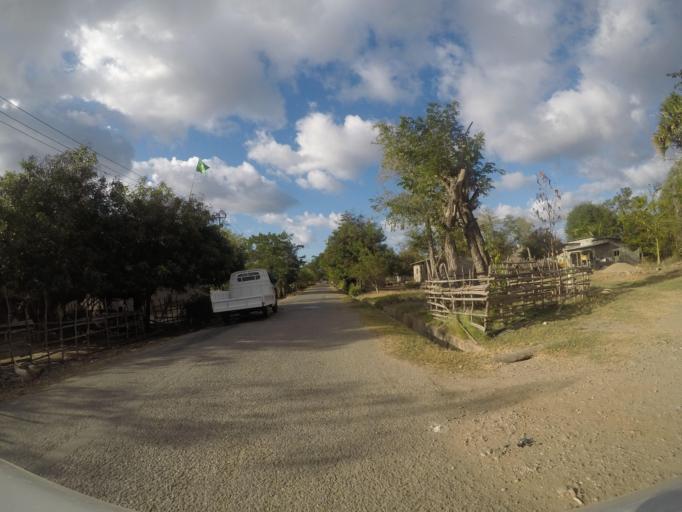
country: TL
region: Lautem
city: Lospalos
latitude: -8.4069
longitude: 126.8294
